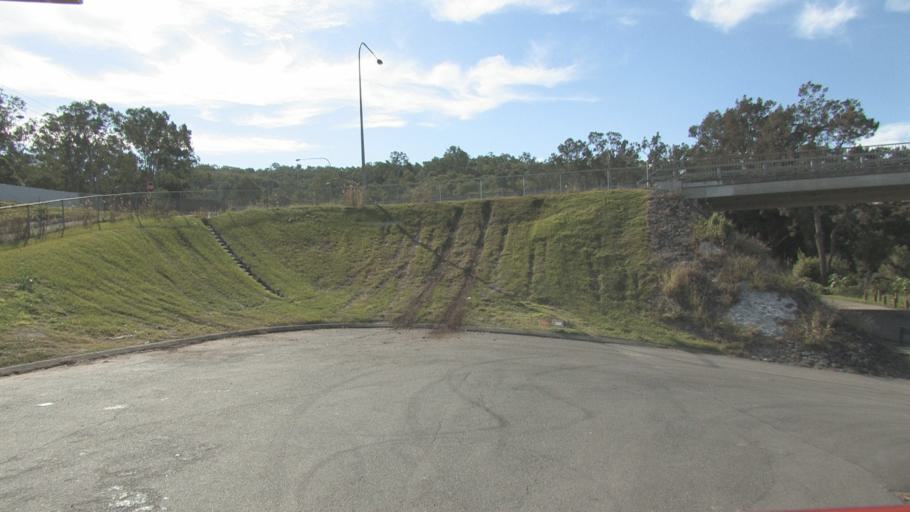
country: AU
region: Queensland
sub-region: Logan
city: Windaroo
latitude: -27.7748
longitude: 153.1861
